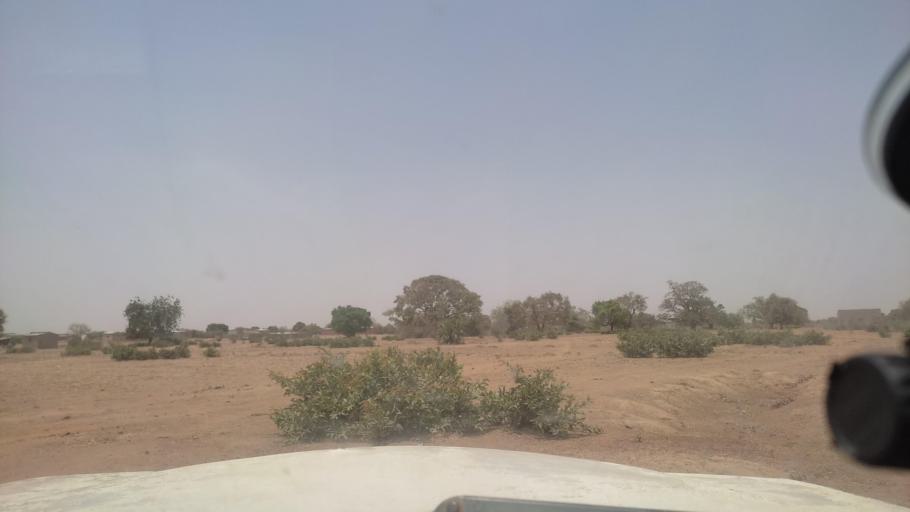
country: BF
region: Est
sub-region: Province du Gourma
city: Fada N'gourma
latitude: 12.0744
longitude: 0.3793
